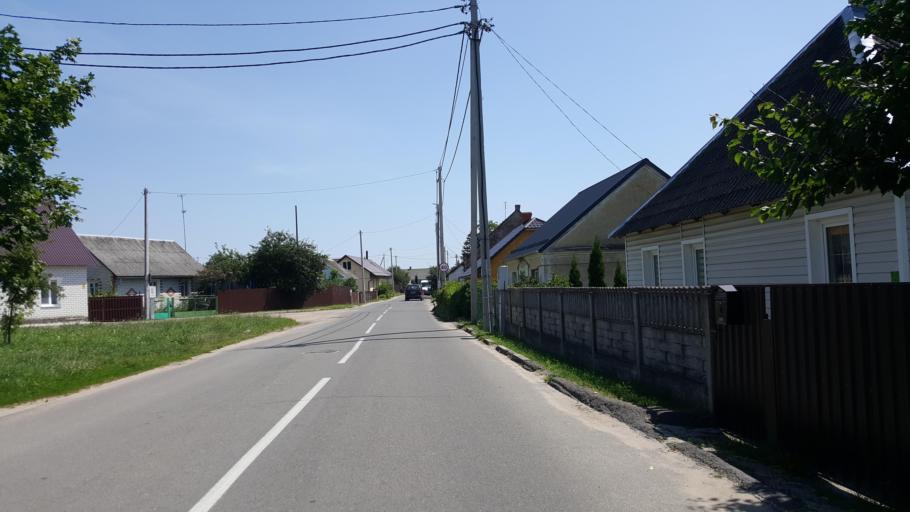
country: BY
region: Brest
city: Vysokaye
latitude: 52.3656
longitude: 23.3793
